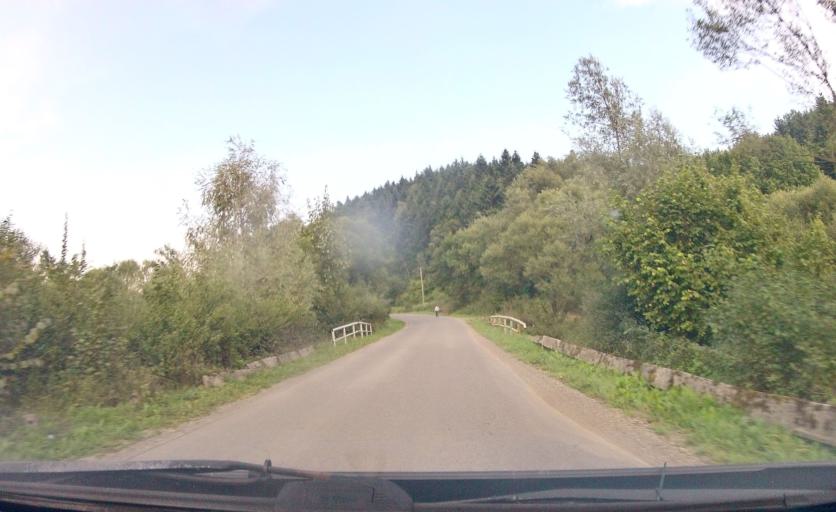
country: PL
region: Subcarpathian Voivodeship
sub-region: Powiat krosnienski
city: Dukla
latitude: 49.5426
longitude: 21.6186
